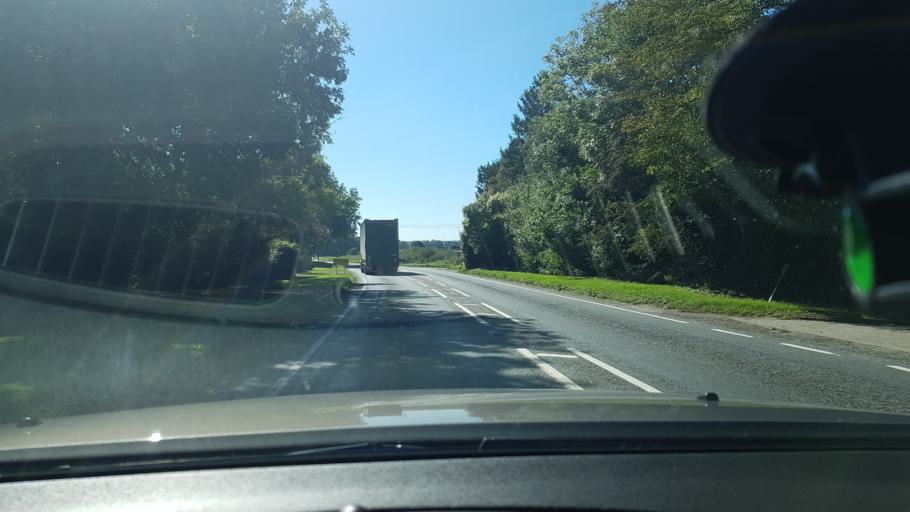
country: GB
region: England
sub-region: Hampshire
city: Four Marks
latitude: 51.0964
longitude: -1.0813
